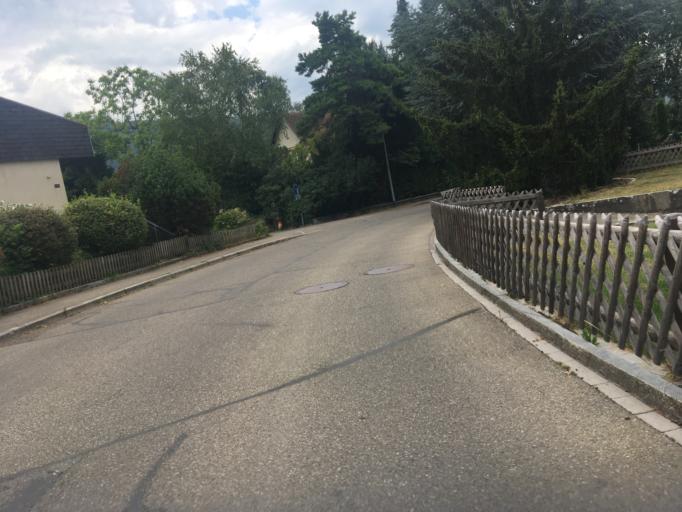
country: CH
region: Bern
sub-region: Biel/Bienne District
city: Nidau
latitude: 47.1220
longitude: 7.2344
